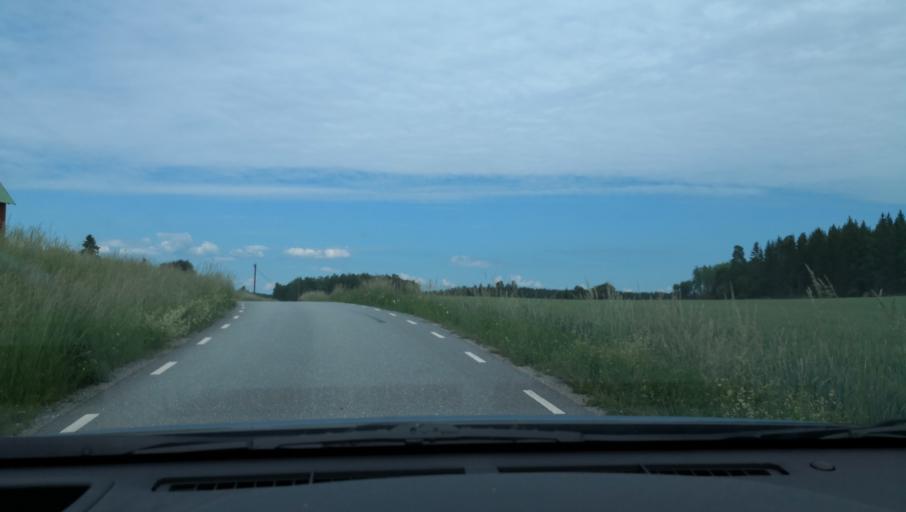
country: SE
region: Uppsala
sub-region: Habo Kommun
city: Balsta
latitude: 59.7050
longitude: 17.4760
